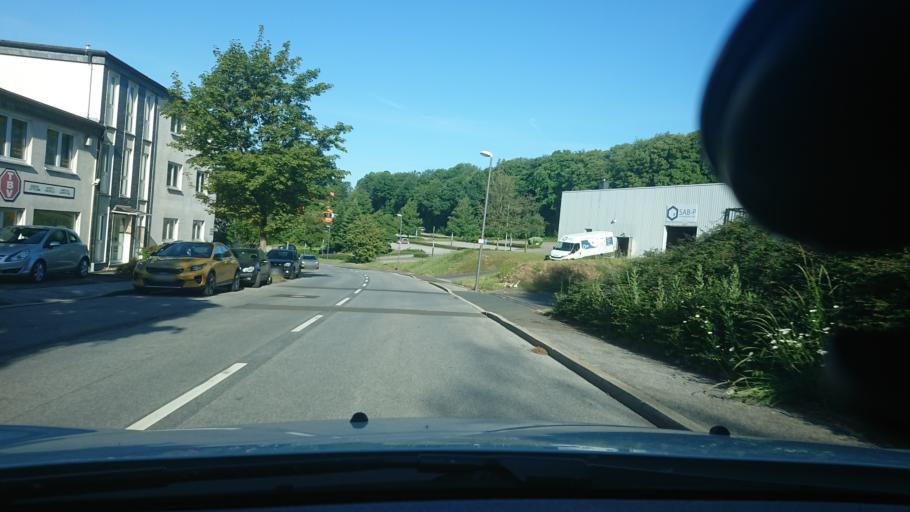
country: DE
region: North Rhine-Westphalia
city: Wermelskirchen
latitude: 51.1468
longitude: 7.2522
